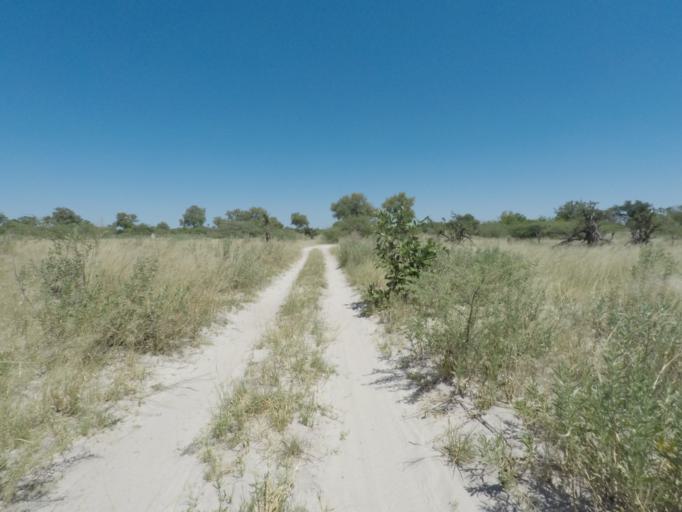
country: BW
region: North West
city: Maun
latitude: -19.4481
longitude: 23.5568
